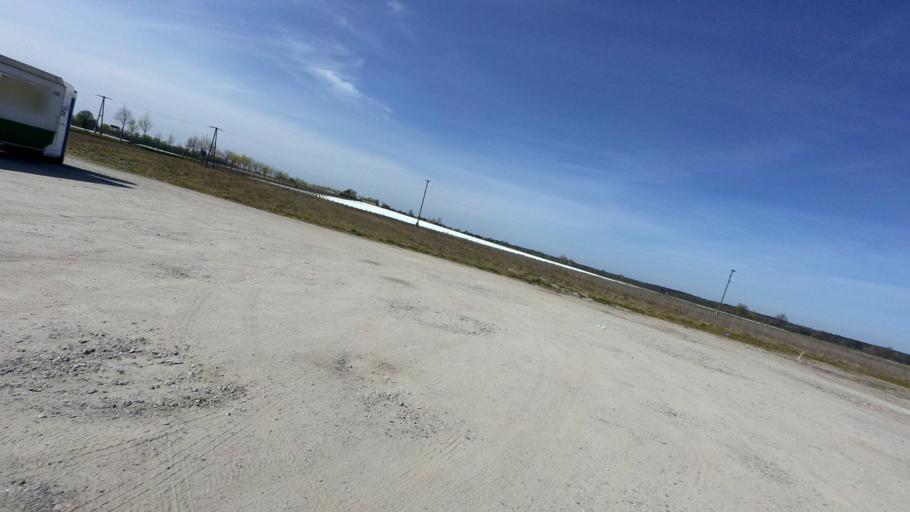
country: DE
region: Brandenburg
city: Tantow
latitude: 53.2771
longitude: 14.3055
